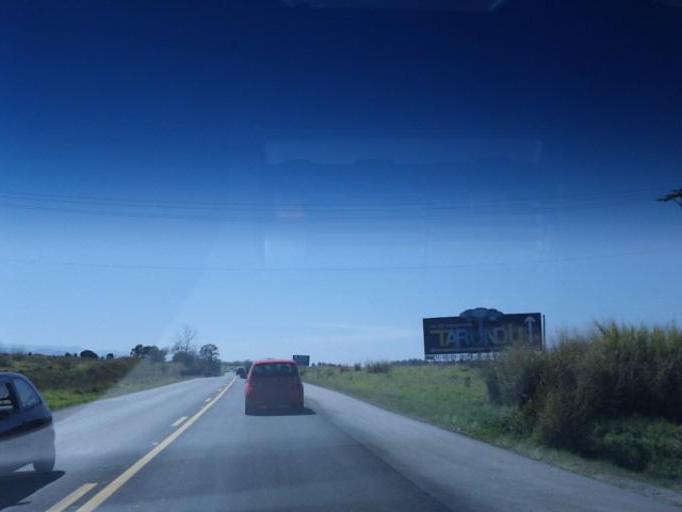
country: BR
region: Sao Paulo
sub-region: Tremembe
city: Tremembe
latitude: -22.9415
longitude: -45.6007
